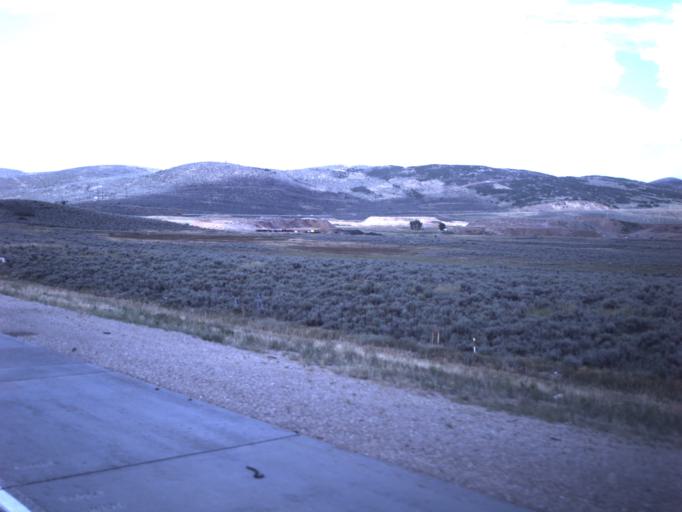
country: US
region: Utah
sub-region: Summit County
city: Park City
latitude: 40.6686
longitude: -111.4594
